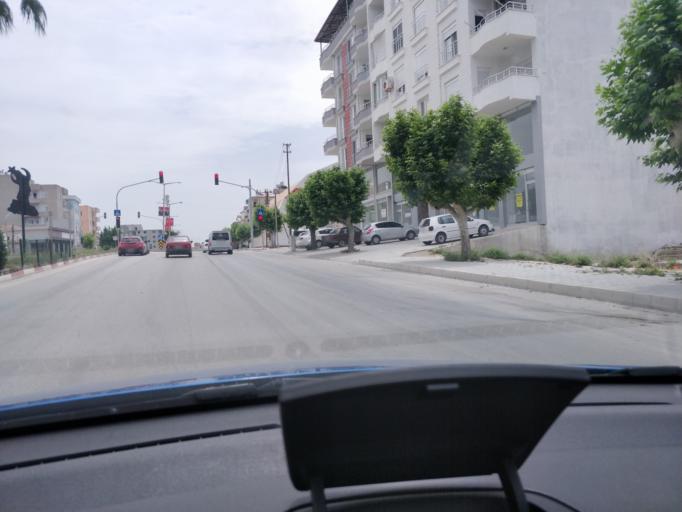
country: TR
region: Mersin
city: Mut
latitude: 36.6380
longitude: 33.4443
